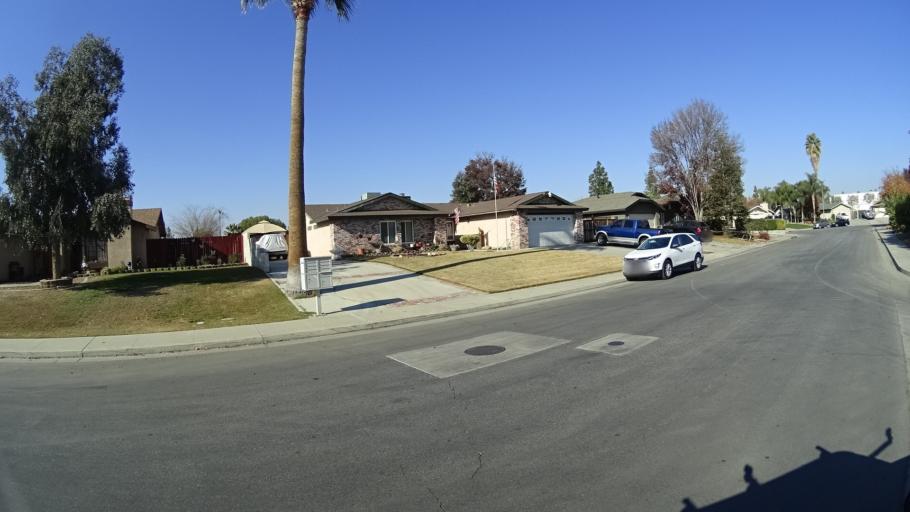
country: US
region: California
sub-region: Kern County
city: Greenfield
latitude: 35.2983
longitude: -119.0383
